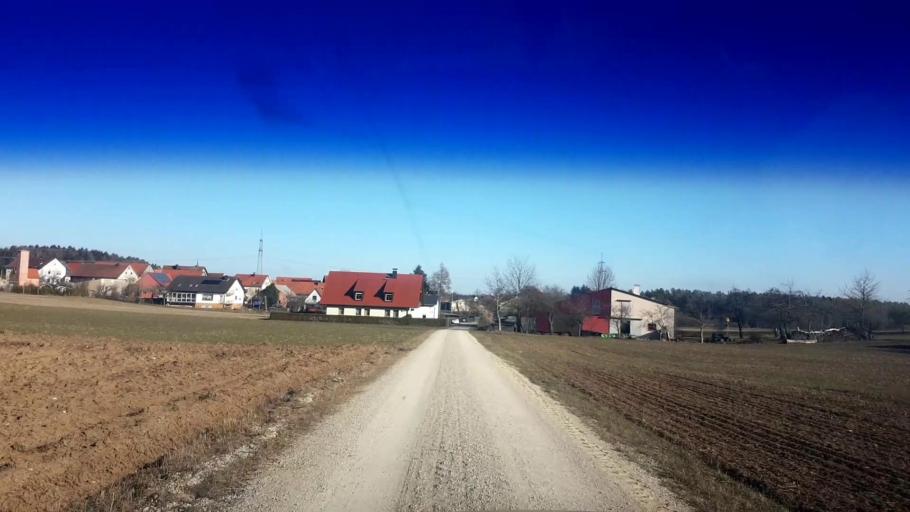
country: DE
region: Bavaria
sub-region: Upper Franconia
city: Poxdorf
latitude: 49.9628
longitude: 11.0957
